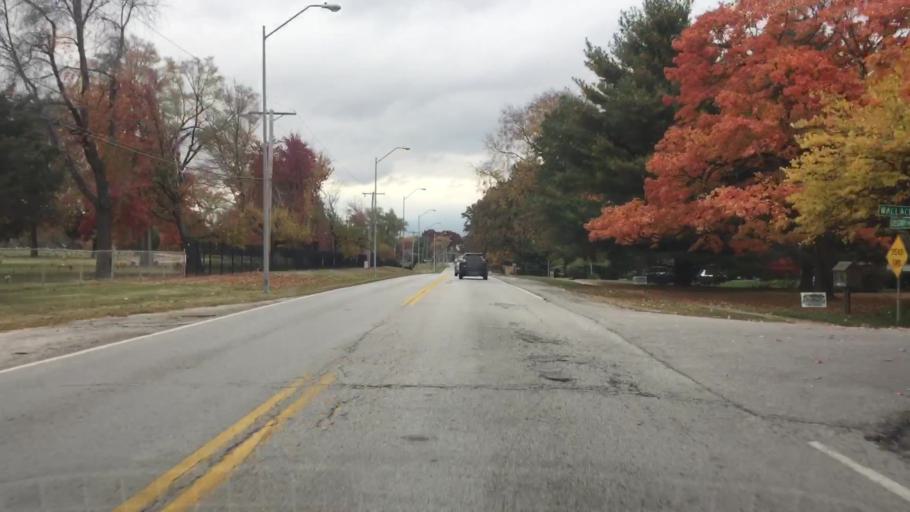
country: US
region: Missouri
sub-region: Jackson County
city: Raytown
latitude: 38.9953
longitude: -94.4887
